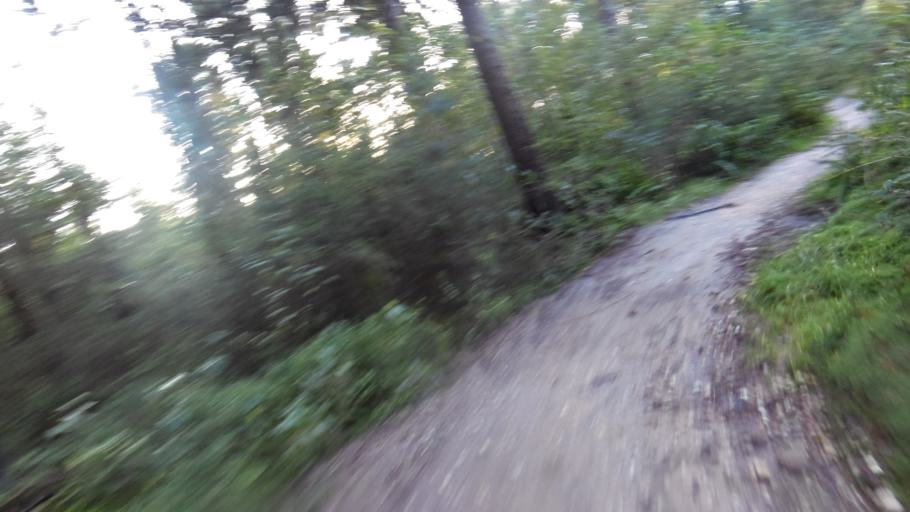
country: NL
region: Utrecht
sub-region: Gemeente Utrechtse Heuvelrug
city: Amerongen
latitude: 51.9979
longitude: 5.4985
